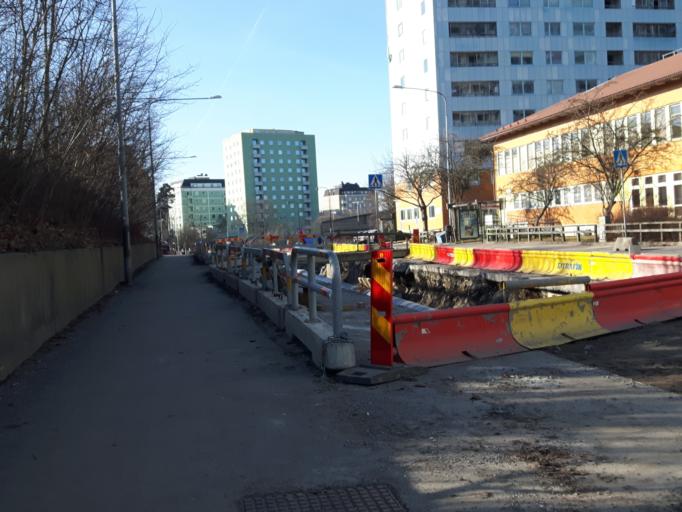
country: SE
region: Stockholm
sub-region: Solna Kommun
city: Solna
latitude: 59.3627
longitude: 18.0097
